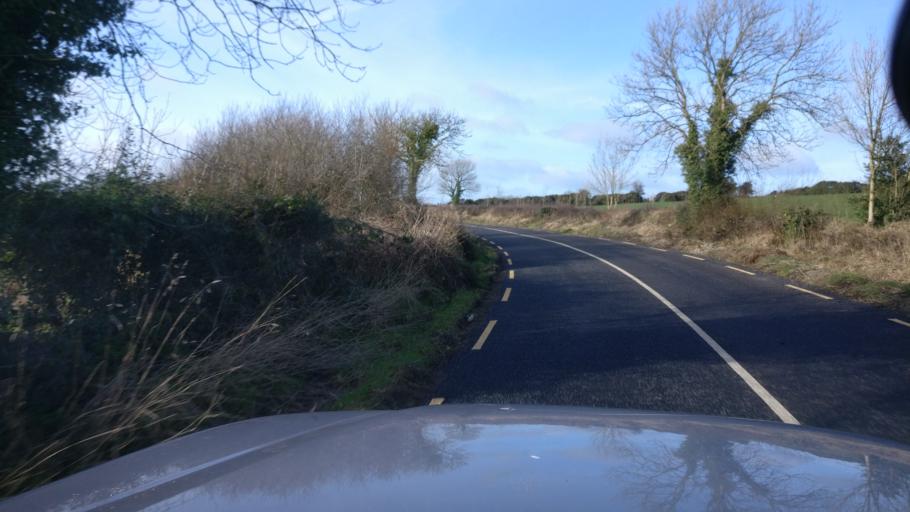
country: IE
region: Leinster
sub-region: Kilkenny
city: Castlecomer
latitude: 52.9030
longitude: -7.1779
